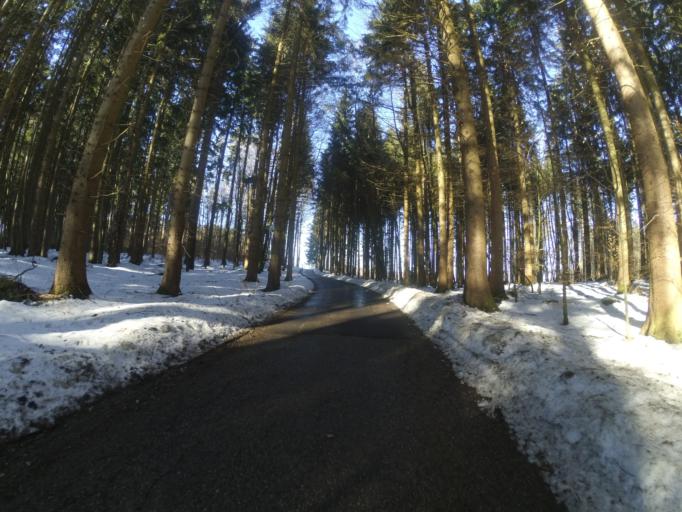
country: DE
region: Bavaria
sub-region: Upper Bavaria
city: Aying
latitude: 47.9369
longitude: 11.8075
